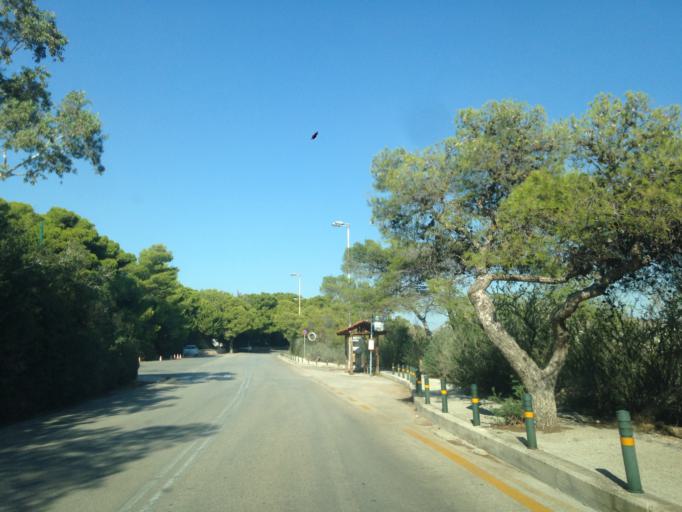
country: GR
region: Attica
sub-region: Nomarchia Anatolikis Attikis
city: Vouliagmeni
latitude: 37.8061
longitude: 23.7736
